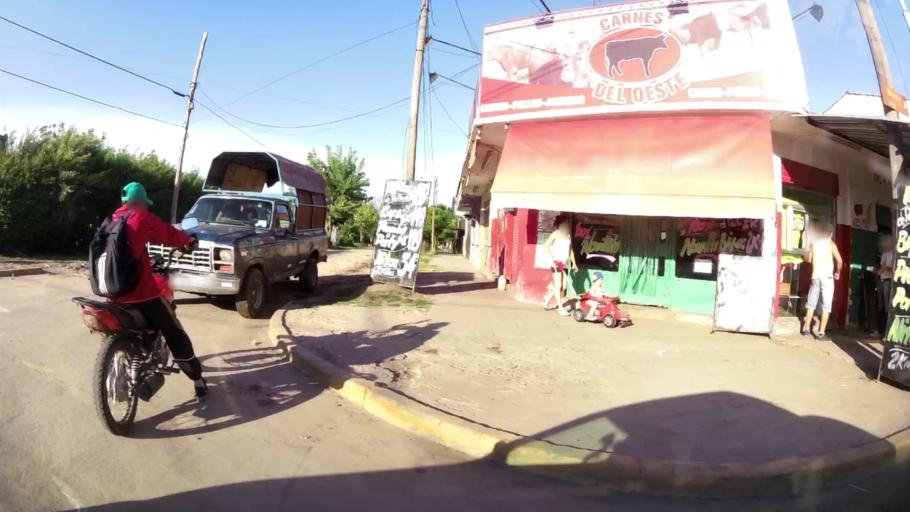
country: AR
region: Buenos Aires
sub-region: Partido de Merlo
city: Merlo
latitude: -34.6904
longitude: -58.7488
